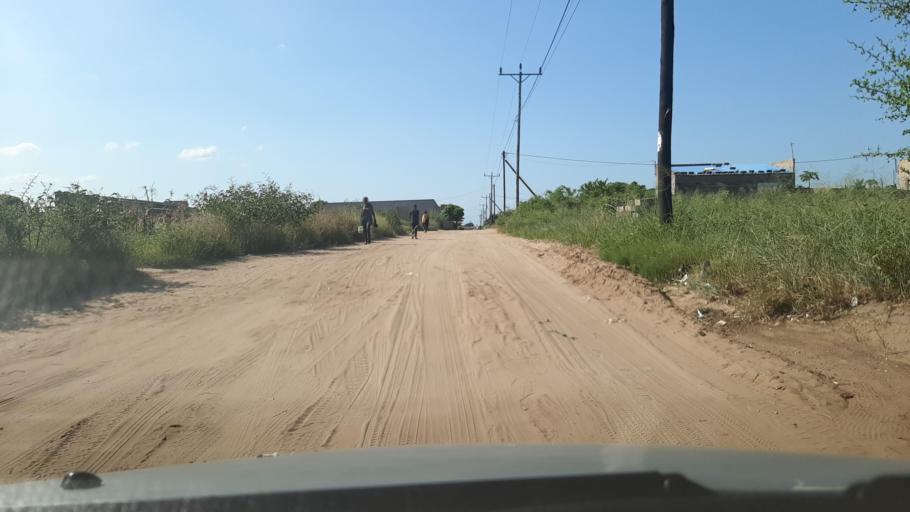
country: MZ
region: Maputo
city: Matola
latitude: -25.8035
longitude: 32.4912
